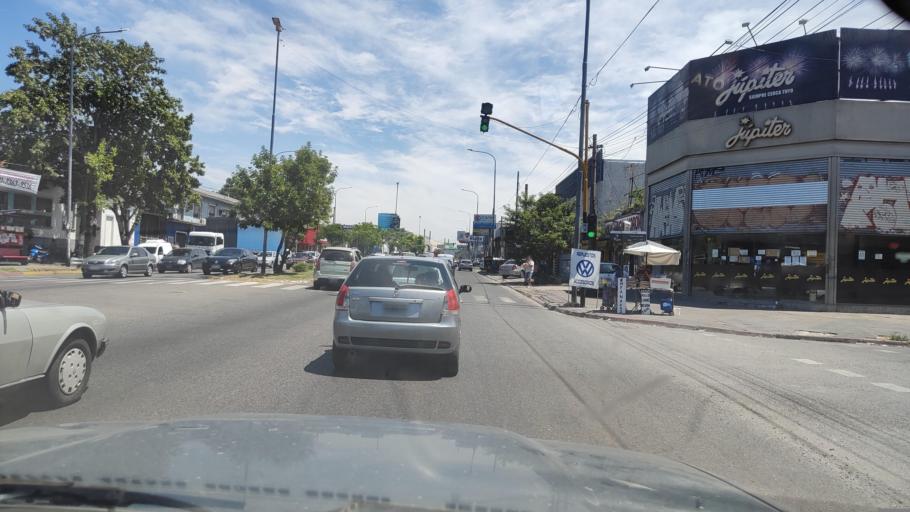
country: AR
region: Buenos Aires
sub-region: Partido de Moron
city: Moron
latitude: -34.6380
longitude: -58.6265
